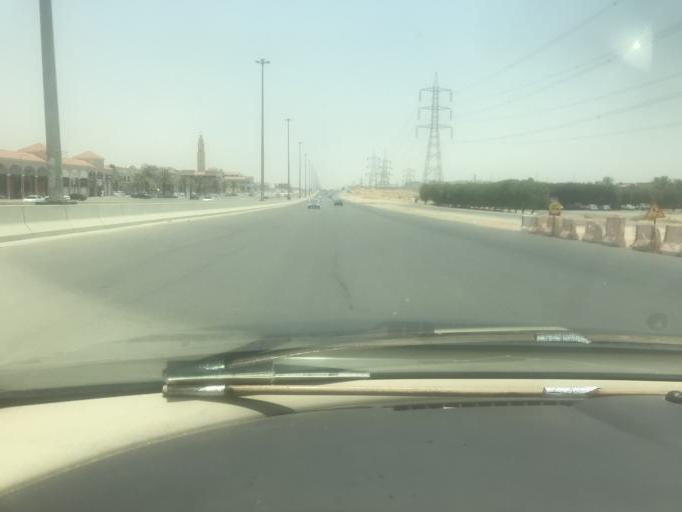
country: SA
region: Ar Riyad
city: Riyadh
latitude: 24.8132
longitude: 46.7242
